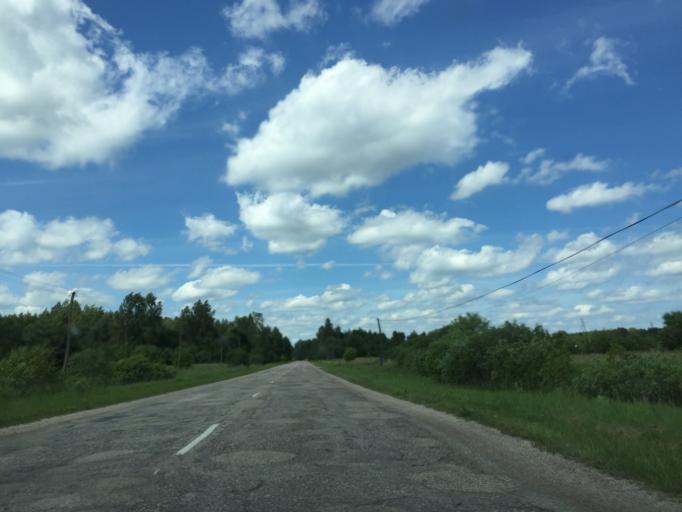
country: LV
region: Engure
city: Smarde
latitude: 56.9649
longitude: 23.3295
